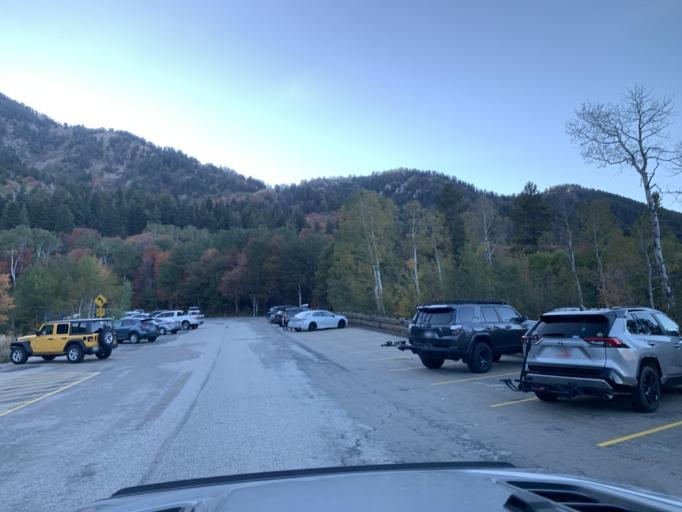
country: US
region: Utah
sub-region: Weber County
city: Uintah
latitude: 41.2185
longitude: -111.8622
